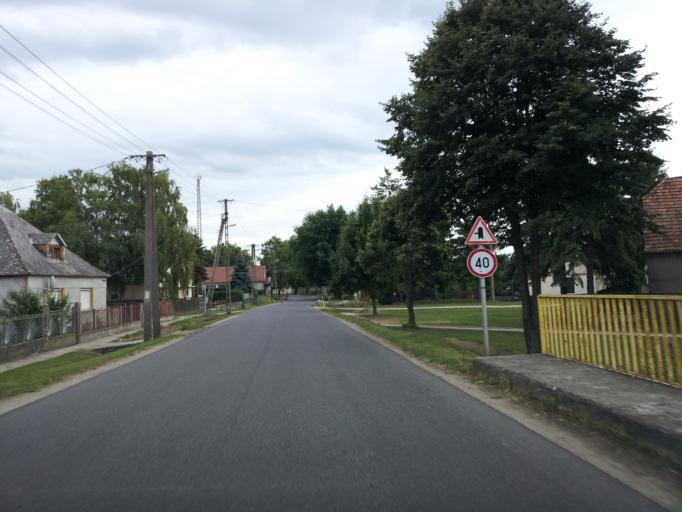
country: HU
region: Veszprem
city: Devecser
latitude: 47.1218
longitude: 17.3760
